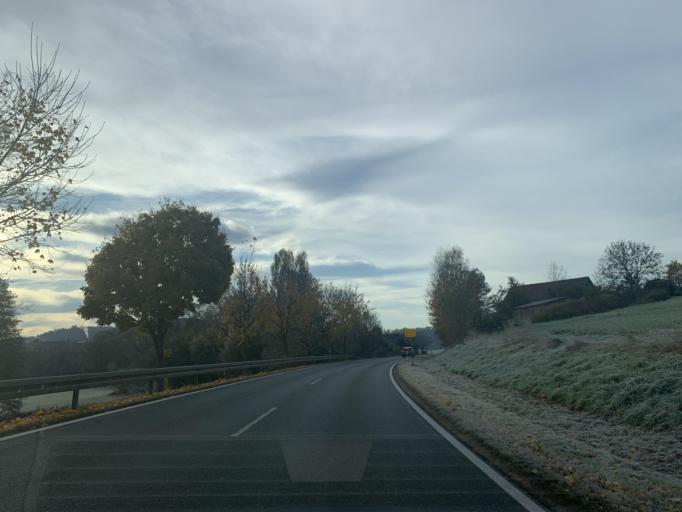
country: DE
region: Bavaria
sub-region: Upper Palatinate
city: Neunburg vorm Wald
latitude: 49.3719
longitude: 12.3788
